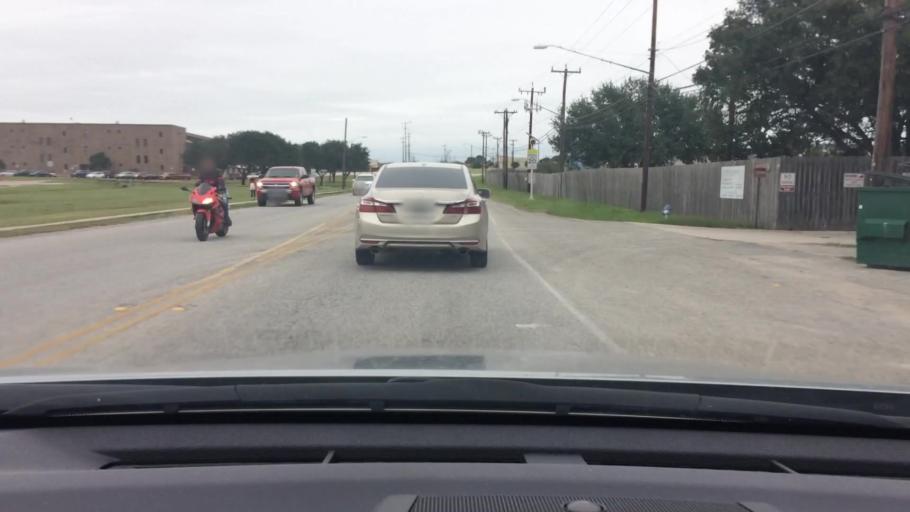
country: US
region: Texas
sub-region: Bexar County
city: Converse
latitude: 29.5093
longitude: -98.2997
